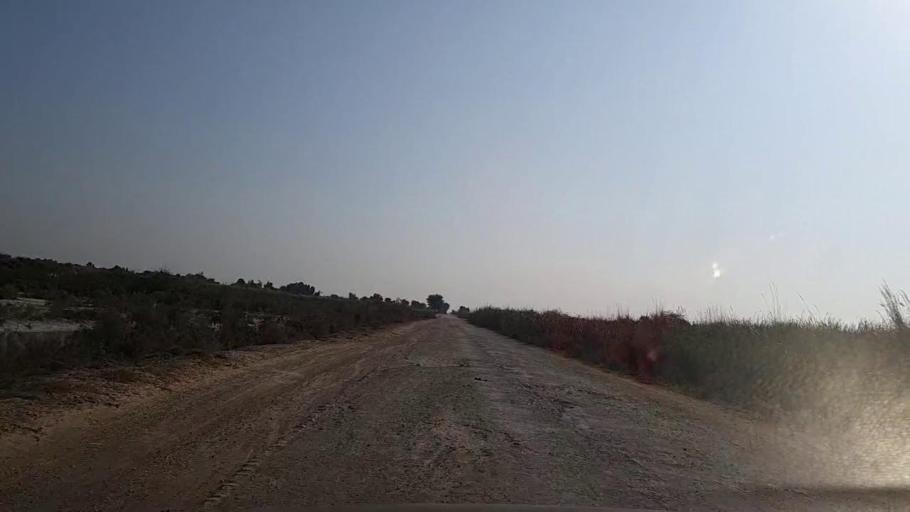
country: PK
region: Sindh
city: Tando Mittha Khan
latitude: 25.9035
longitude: 69.0772
